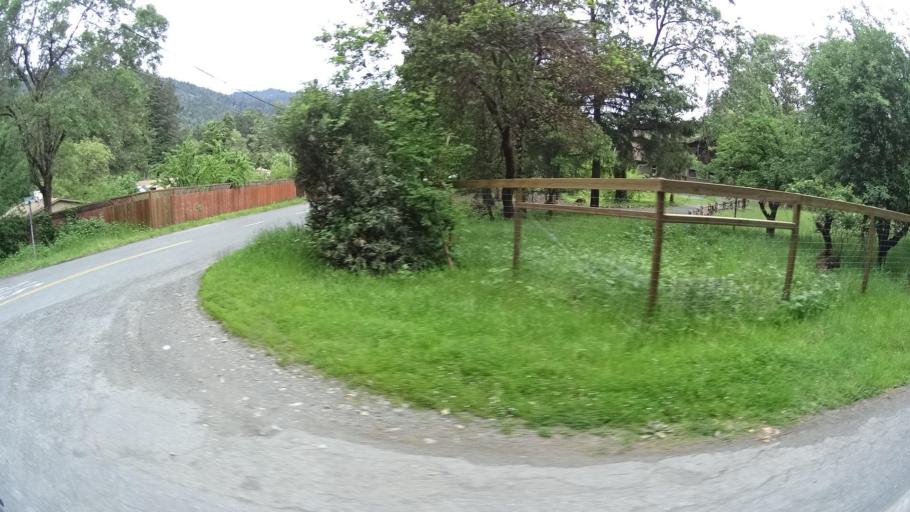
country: US
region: California
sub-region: Humboldt County
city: Willow Creek
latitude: 40.9686
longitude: -123.6313
